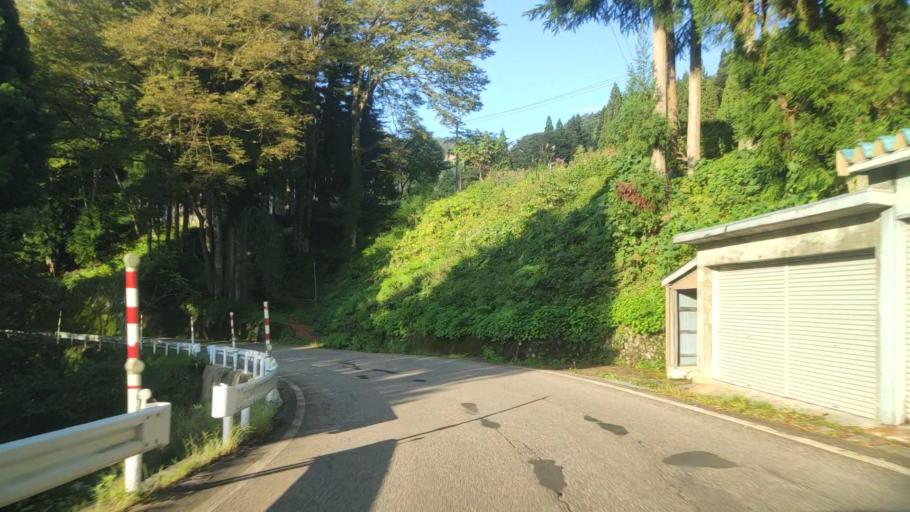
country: JP
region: Toyama
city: Yatsuomachi-higashikumisaka
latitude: 36.4769
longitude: 137.0316
